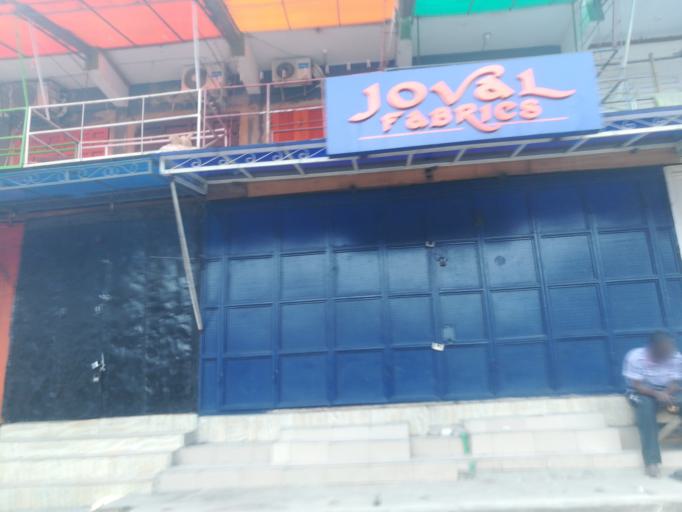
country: NG
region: Lagos
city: Lagos
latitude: 6.4566
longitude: 3.3843
